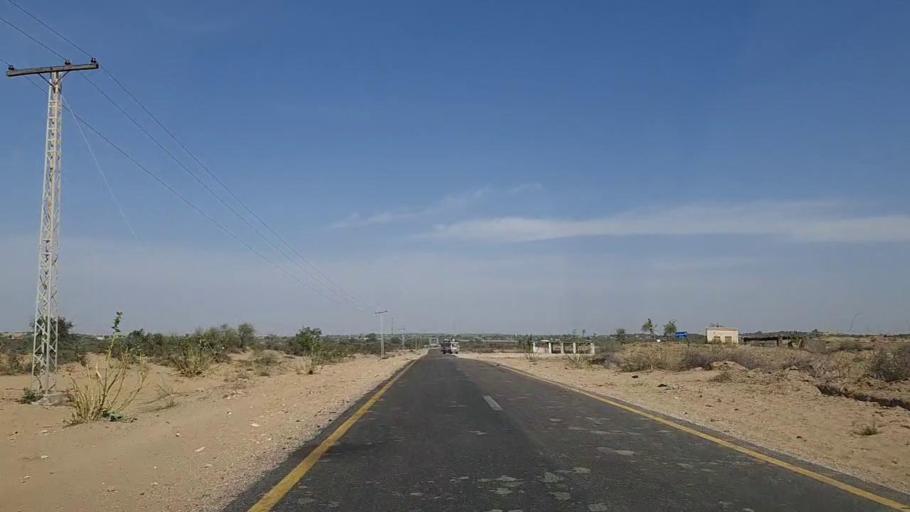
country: PK
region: Sindh
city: Mithi
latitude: 24.9614
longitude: 69.9089
